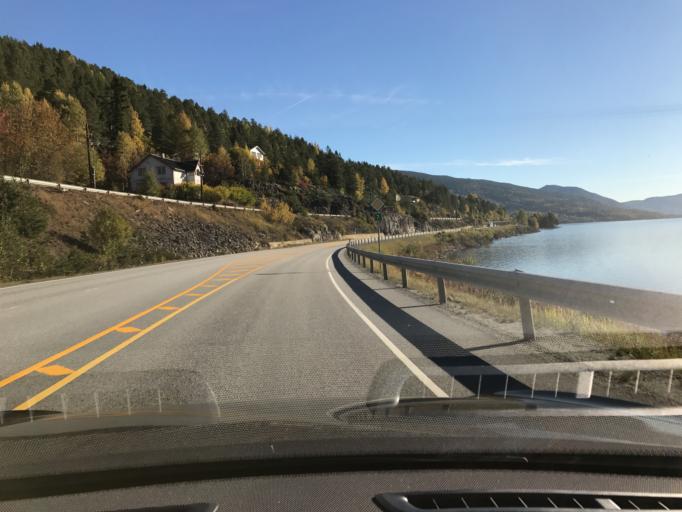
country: NO
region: Buskerud
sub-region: Fla
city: Fla
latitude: 60.3810
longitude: 9.6127
